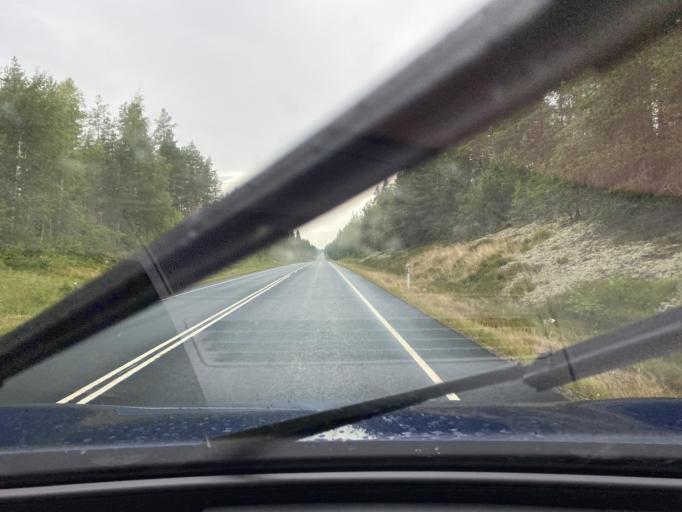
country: FI
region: Central Ostrobothnia
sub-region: Kaustinen
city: Veteli
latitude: 63.4135
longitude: 23.9518
